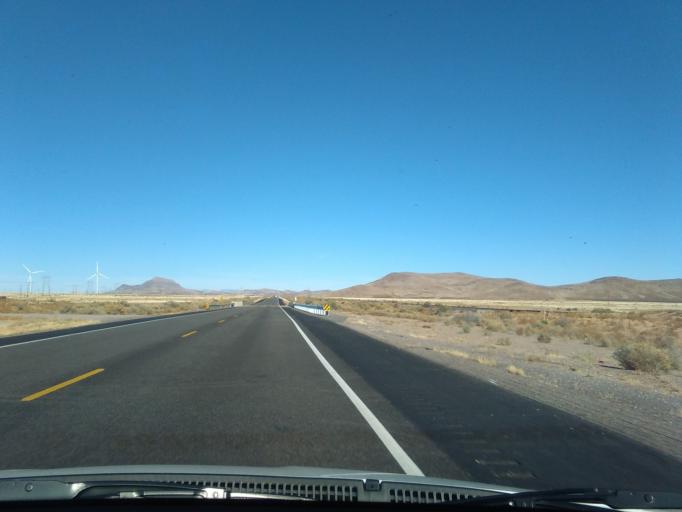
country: US
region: New Mexico
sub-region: Luna County
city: Deming
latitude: 32.5132
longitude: -107.5029
